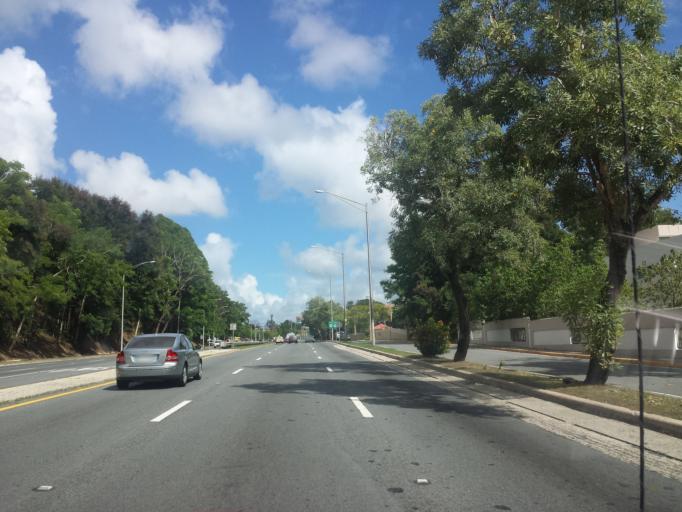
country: PR
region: Trujillo Alto
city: Trujillo Alto
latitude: 18.3575
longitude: -66.0576
